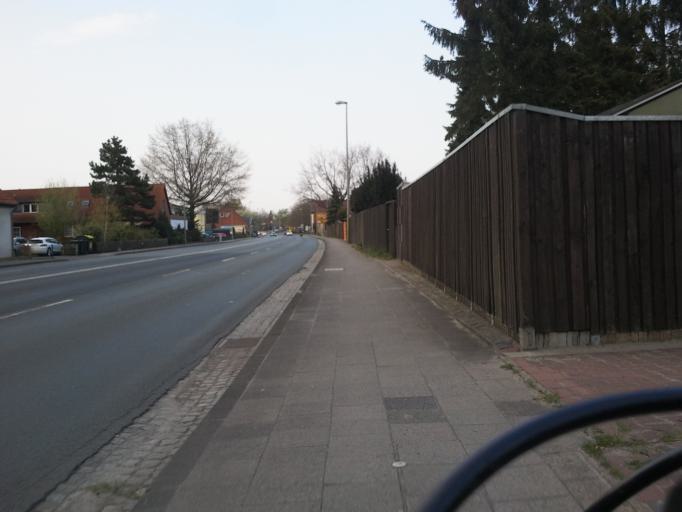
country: DE
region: Lower Saxony
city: Nienburg
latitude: 52.6273
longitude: 9.2147
